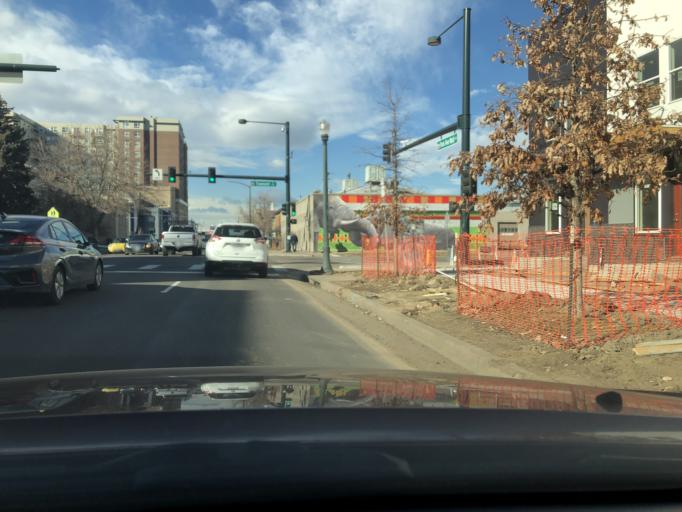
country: US
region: Colorado
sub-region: Denver County
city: Denver
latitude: 39.7495
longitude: -104.9807
